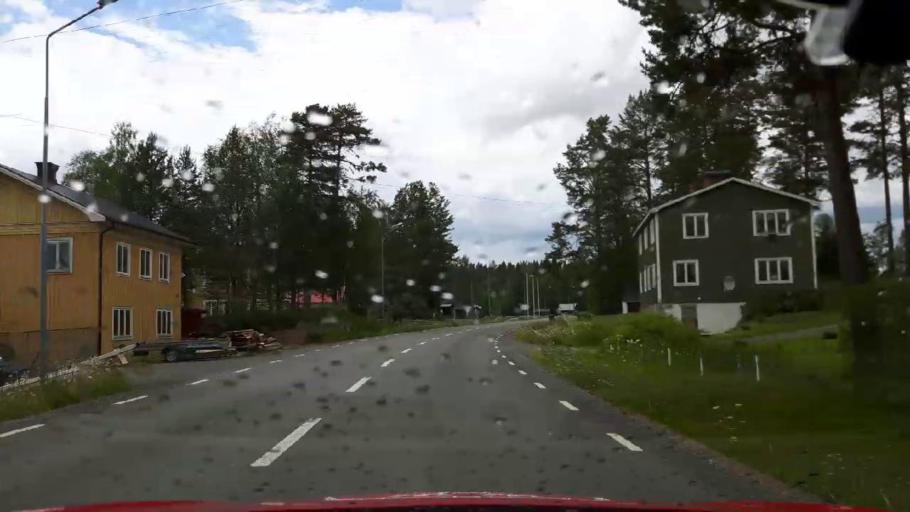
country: SE
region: Jaemtland
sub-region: Krokoms Kommun
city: Krokom
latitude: 63.5652
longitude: 14.2725
